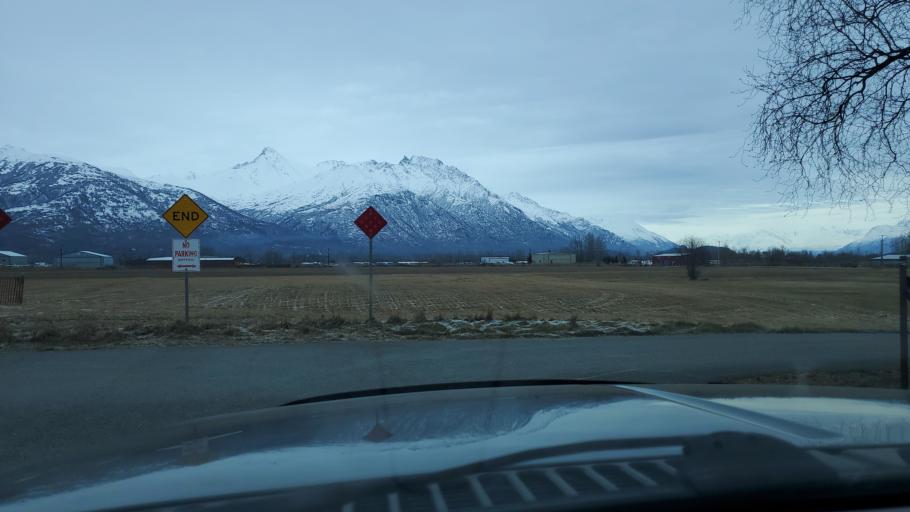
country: US
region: Alaska
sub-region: Matanuska-Susitna Borough
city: Palmer
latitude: 61.6011
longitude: -149.1014
